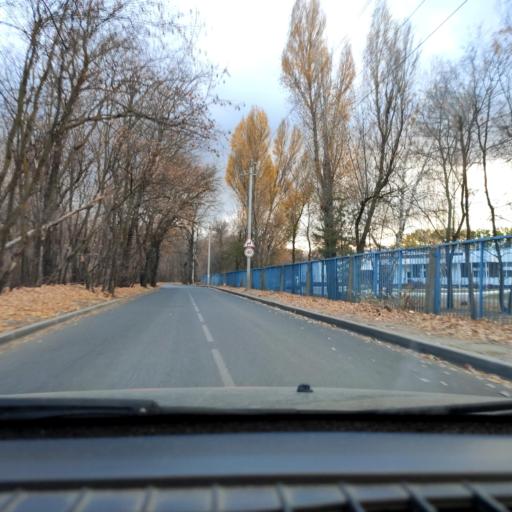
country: RU
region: Samara
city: Tol'yatti
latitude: 53.5217
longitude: 49.3327
